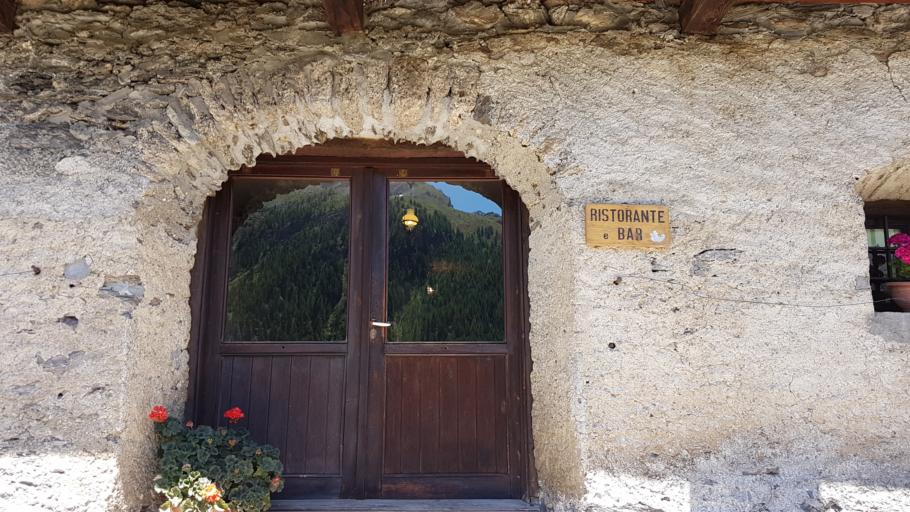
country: IT
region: Piedmont
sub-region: Provincia di Torino
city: Prali
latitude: 44.8873
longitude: 6.9601
